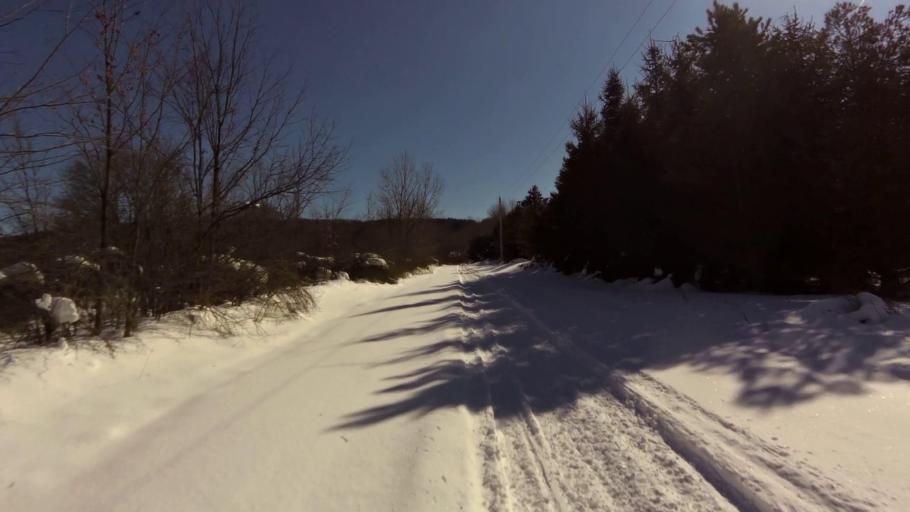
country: US
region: New York
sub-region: Allegany County
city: Cuba
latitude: 42.3315
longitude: -78.3031
